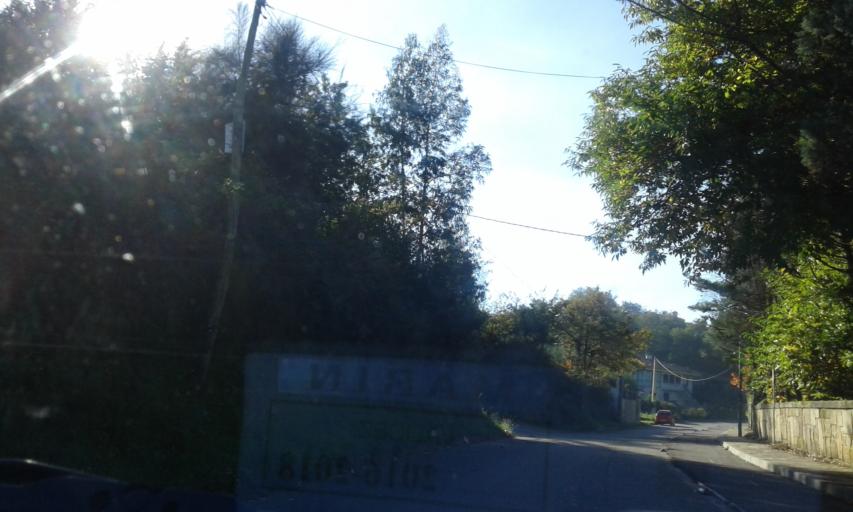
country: ES
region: Galicia
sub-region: Provincia de Pontevedra
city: Marin
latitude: 42.3820
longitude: -8.7248
